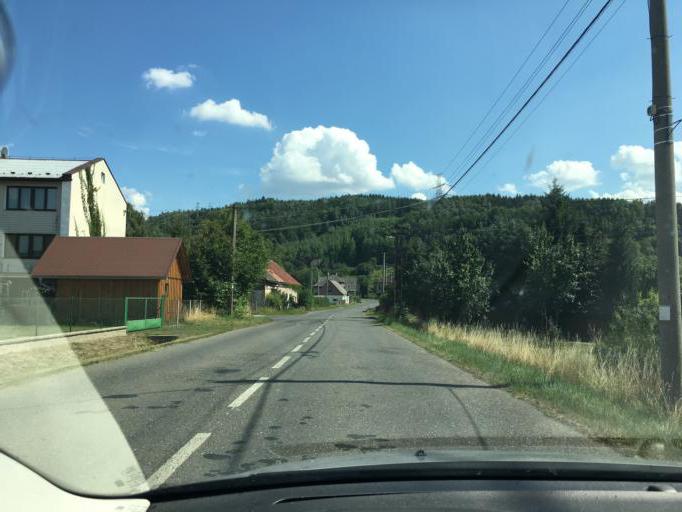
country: CZ
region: Liberecky
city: Hodkovice nad Mohelkou
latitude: 50.6549
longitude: 15.1066
